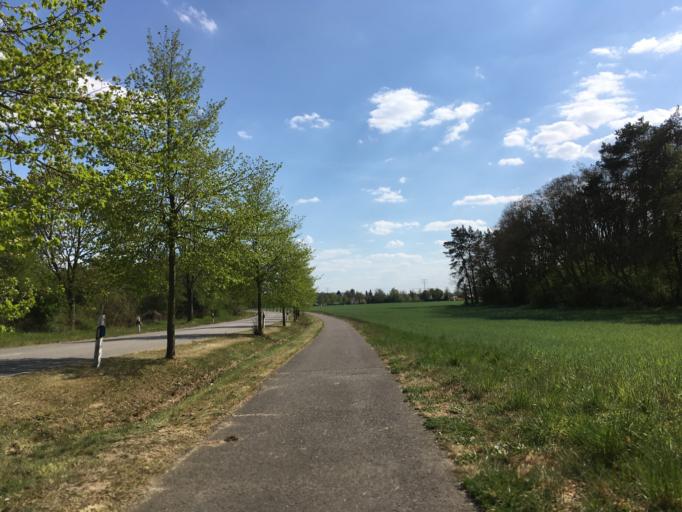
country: DE
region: Brandenburg
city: Ahrensfelde
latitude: 52.5895
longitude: 13.5644
